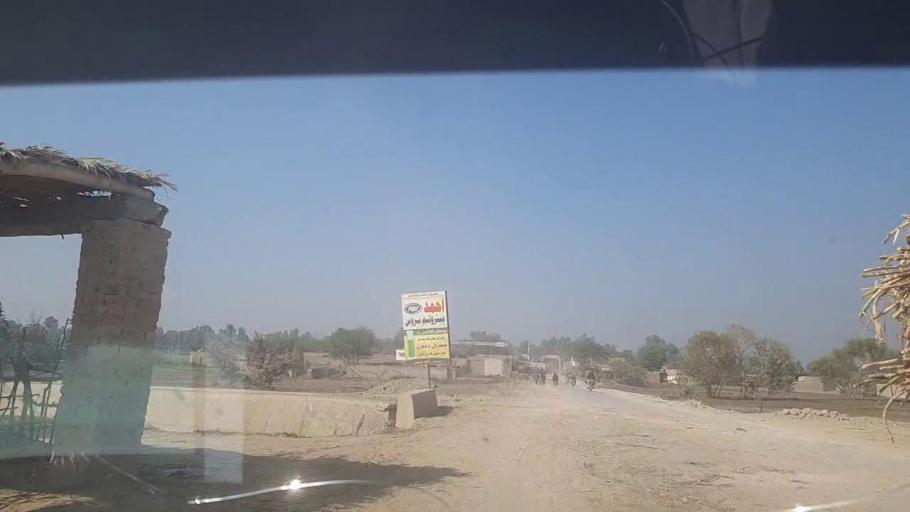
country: PK
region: Sindh
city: Kot Diji
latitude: 27.4291
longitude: 68.6539
